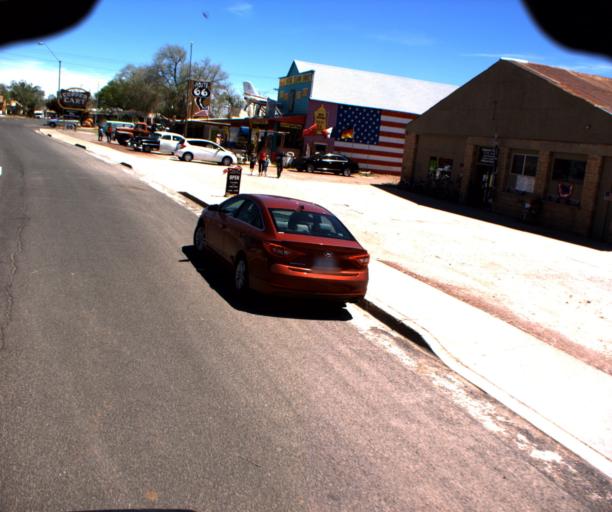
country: US
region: Arizona
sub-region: Mohave County
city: Peach Springs
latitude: 35.3268
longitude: -112.8765
